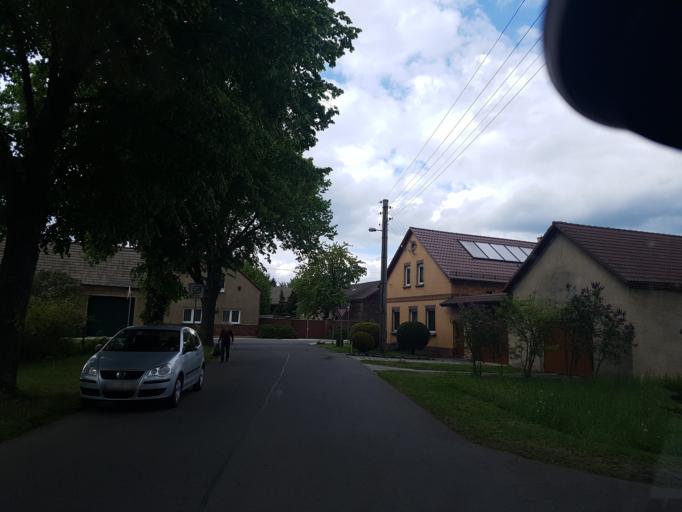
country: DE
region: Brandenburg
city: Neupetershain
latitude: 51.5814
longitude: 14.0948
